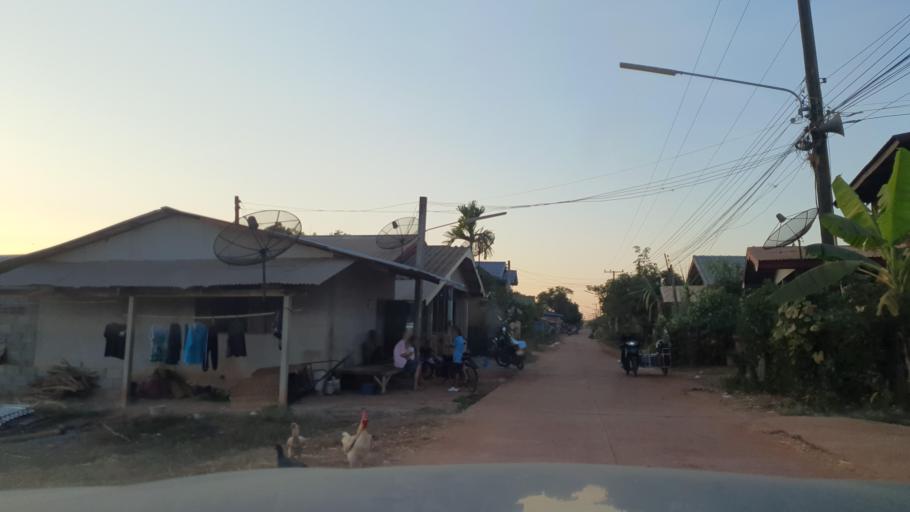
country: TH
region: Nakhon Phanom
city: Ban Phaeng
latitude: 17.8280
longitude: 104.2671
